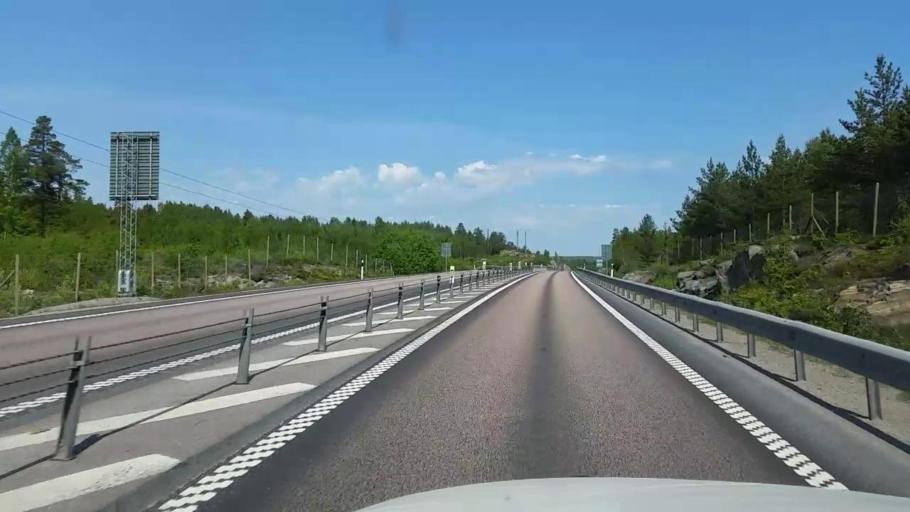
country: SE
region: Gaevleborg
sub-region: Hudiksvalls Kommun
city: Hudiksvall
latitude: 61.7327
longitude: 17.0667
